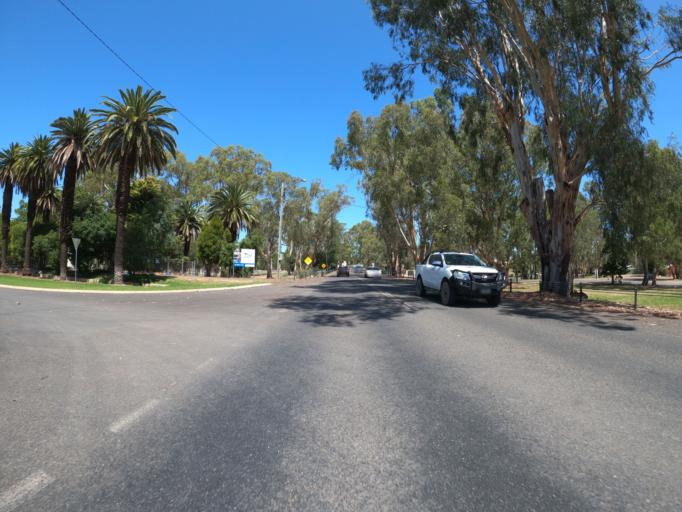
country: AU
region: New South Wales
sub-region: Corowa Shire
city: Corowa
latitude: -36.0043
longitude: 146.3944
